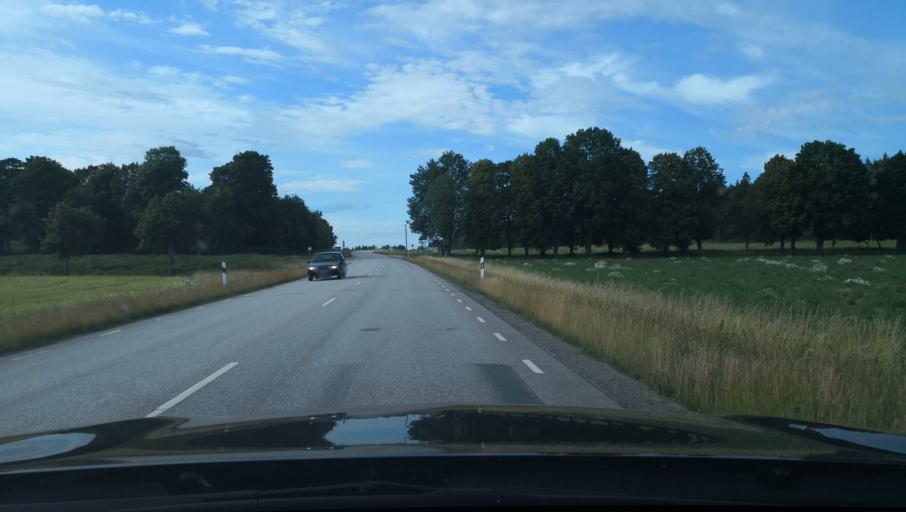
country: SE
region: Uppsala
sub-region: Habo Kommun
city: Balsta
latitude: 59.6158
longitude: 17.4994
